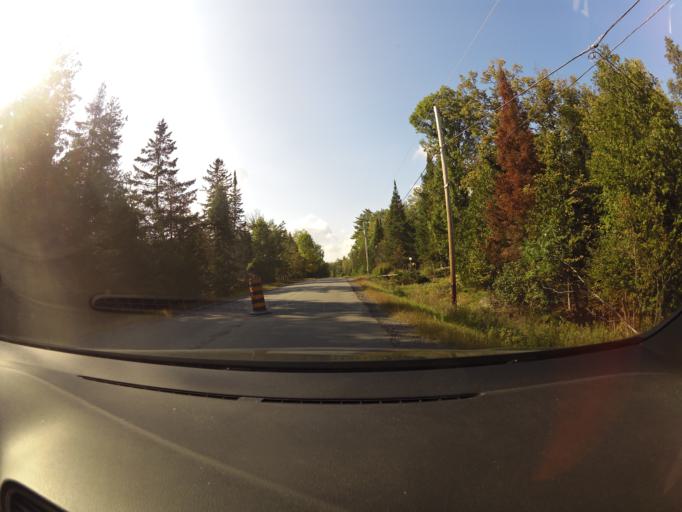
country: CA
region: Ontario
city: Arnprior
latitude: 45.4611
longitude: -76.2781
